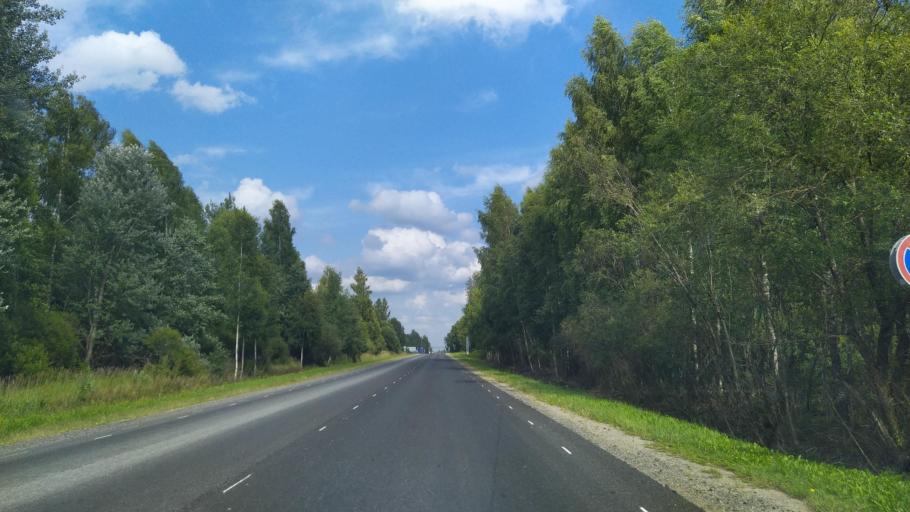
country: RU
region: Pskov
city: Porkhov
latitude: 57.7543
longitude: 29.5193
